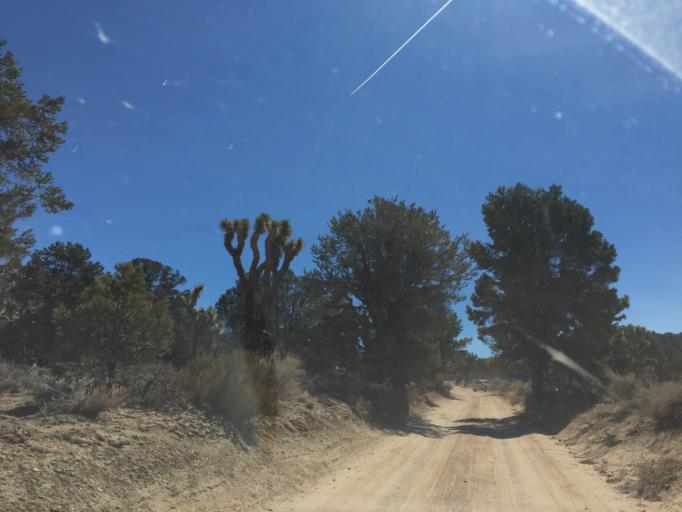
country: US
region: California
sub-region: San Bernardino County
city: Big Bear City
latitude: 34.2469
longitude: -116.7036
